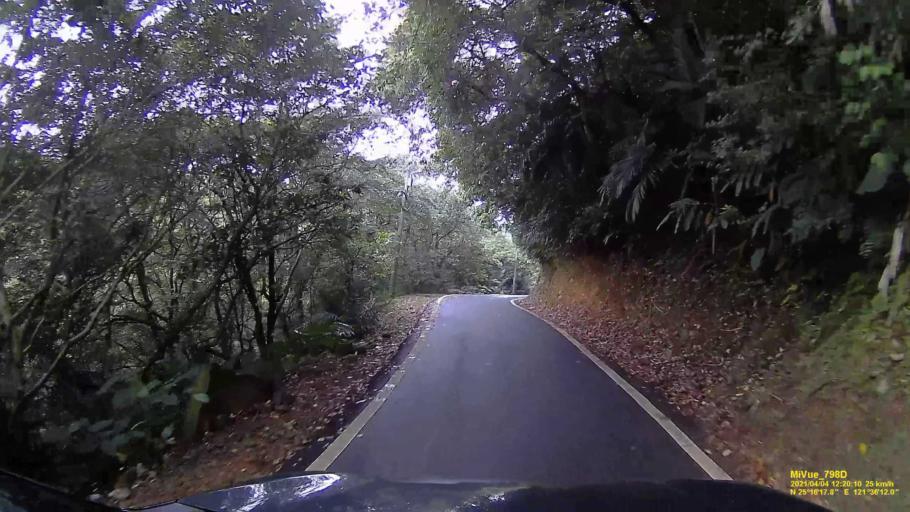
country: TW
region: Taiwan
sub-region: Keelung
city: Keelung
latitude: 25.2718
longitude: 121.6033
